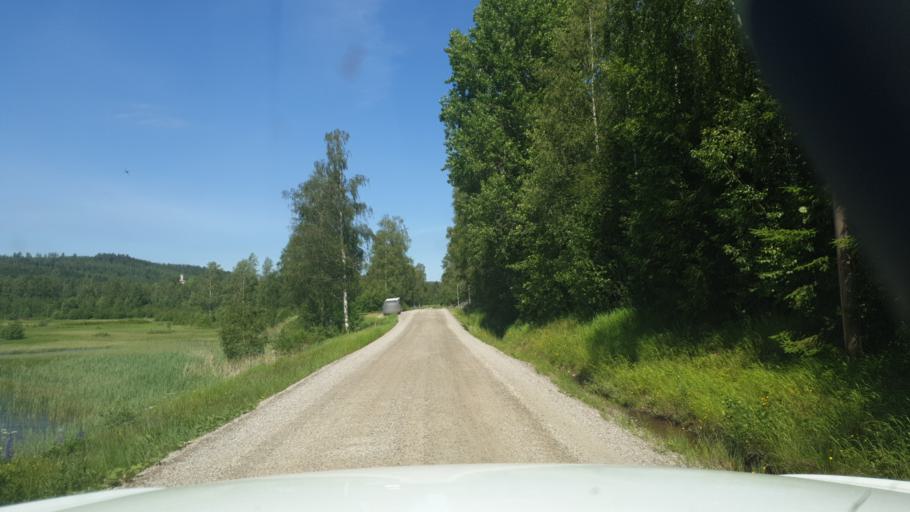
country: SE
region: Vaermland
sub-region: Arvika Kommun
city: Arvika
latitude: 59.7447
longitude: 12.8306
